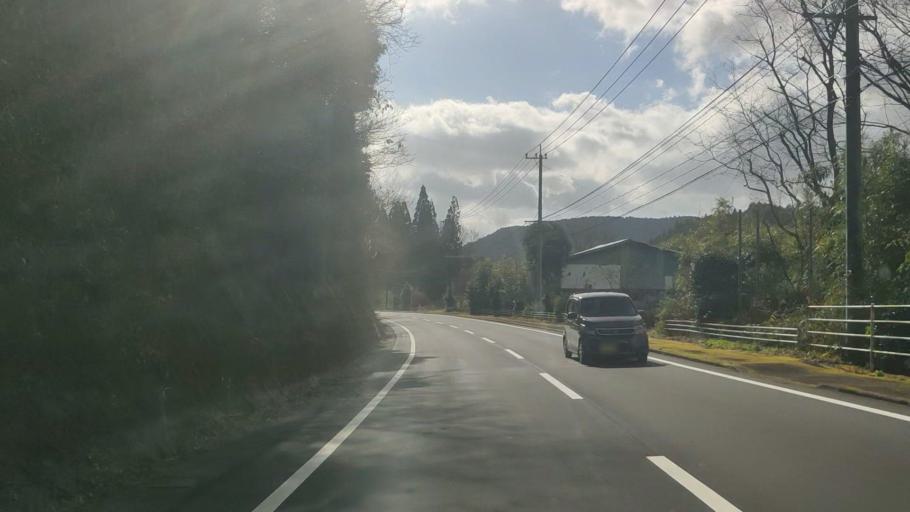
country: JP
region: Kagoshima
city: Okuchi-shinohara
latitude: 31.9858
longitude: 130.7430
